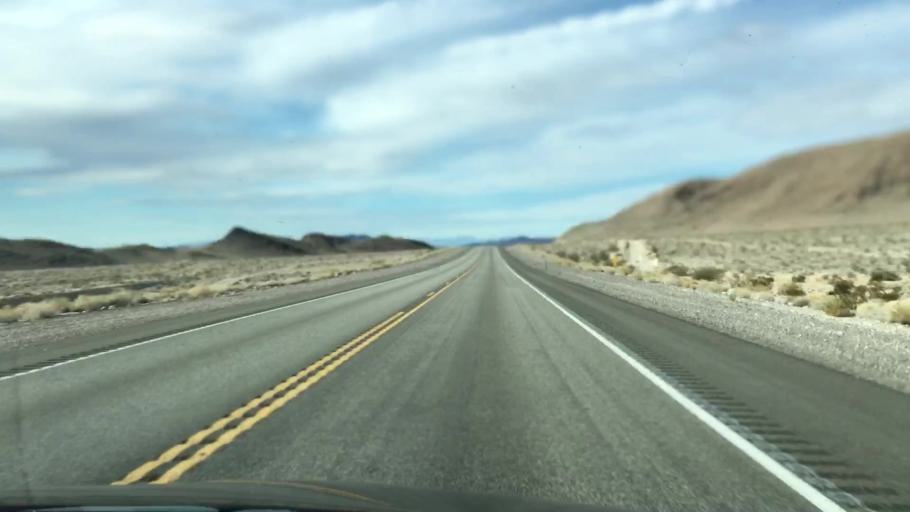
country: US
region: Nevada
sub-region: Nye County
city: Pahrump
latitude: 36.5790
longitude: -116.1981
